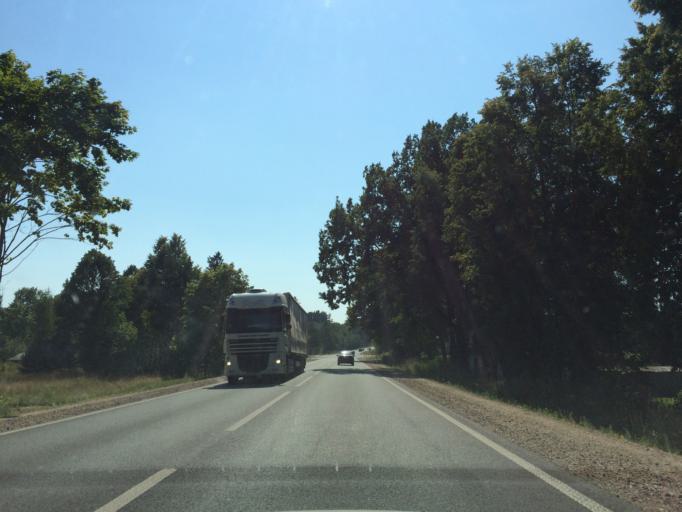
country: LV
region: Rezekne
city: Rezekne
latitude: 56.3693
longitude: 27.1870
